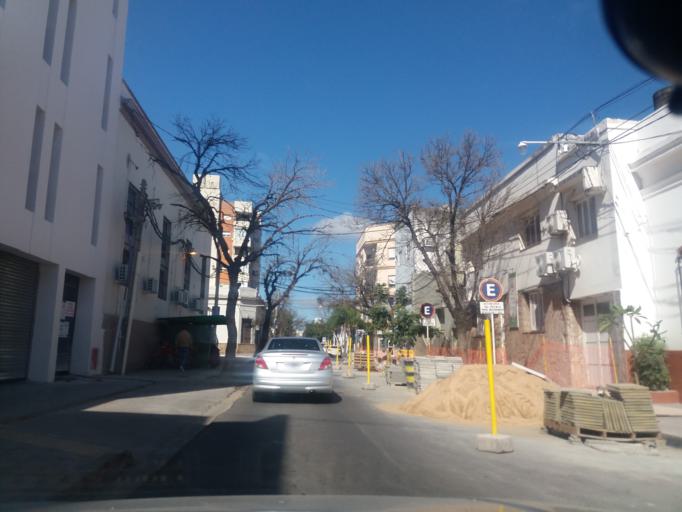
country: AR
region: Corrientes
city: Corrientes
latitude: -27.4718
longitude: -58.8349
